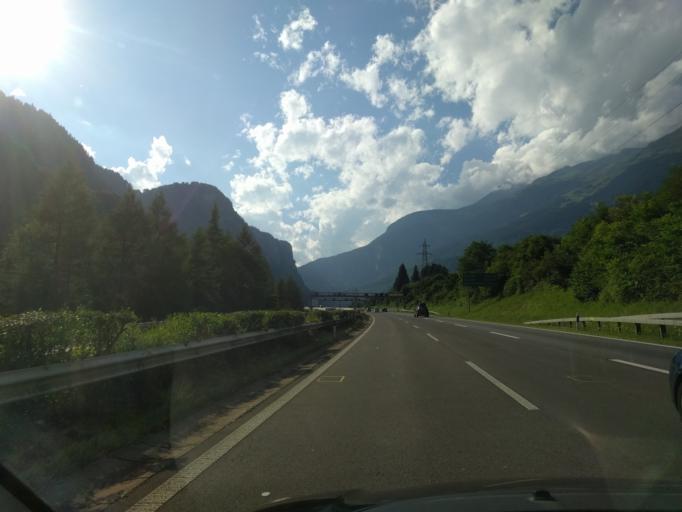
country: CH
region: Ticino
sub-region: Leventina District
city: Faido
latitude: 46.4720
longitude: 8.8094
